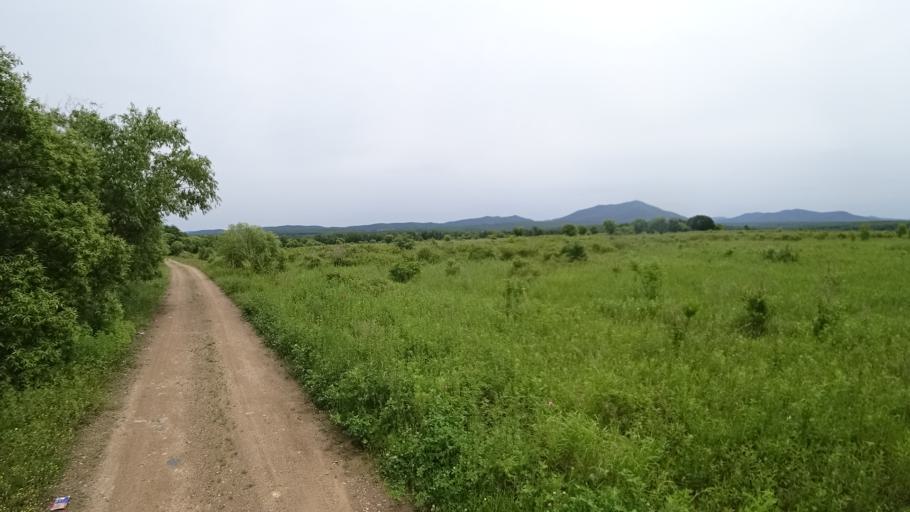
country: RU
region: Primorskiy
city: Arsen'yev
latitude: 44.1833
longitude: 133.3159
